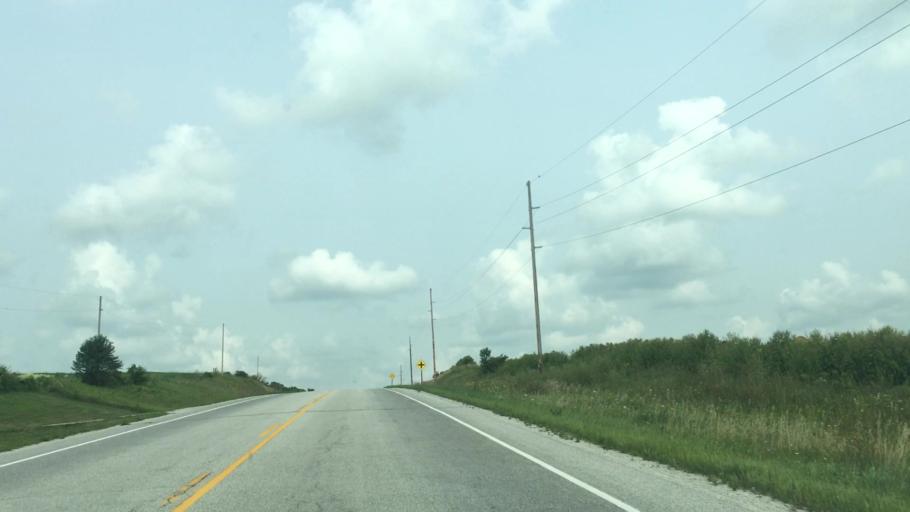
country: US
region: Minnesota
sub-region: Fillmore County
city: Harmony
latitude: 43.5775
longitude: -91.9299
